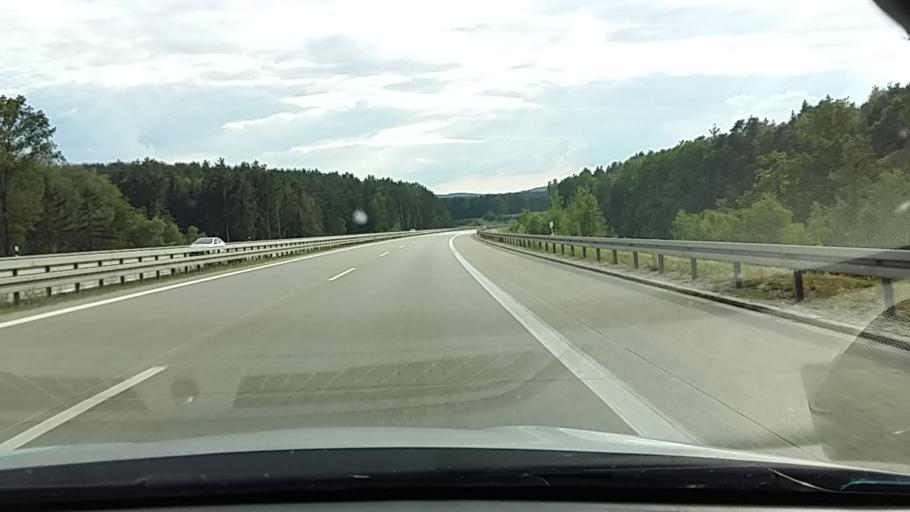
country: DE
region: Bavaria
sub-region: Upper Palatinate
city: Stulln
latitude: 49.4522
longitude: 12.1230
